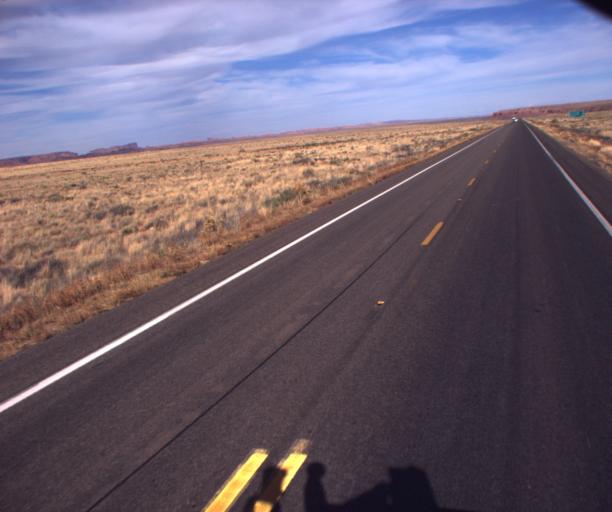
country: US
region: Arizona
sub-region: Navajo County
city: Kayenta
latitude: 36.7337
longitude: -110.0964
